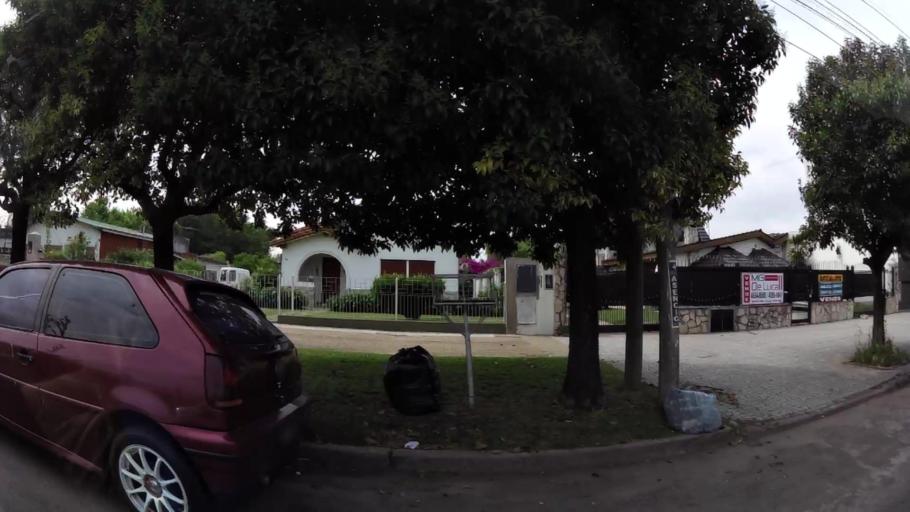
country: AR
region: Buenos Aires F.D.
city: Villa Lugano
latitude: -34.6898
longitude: -58.4976
